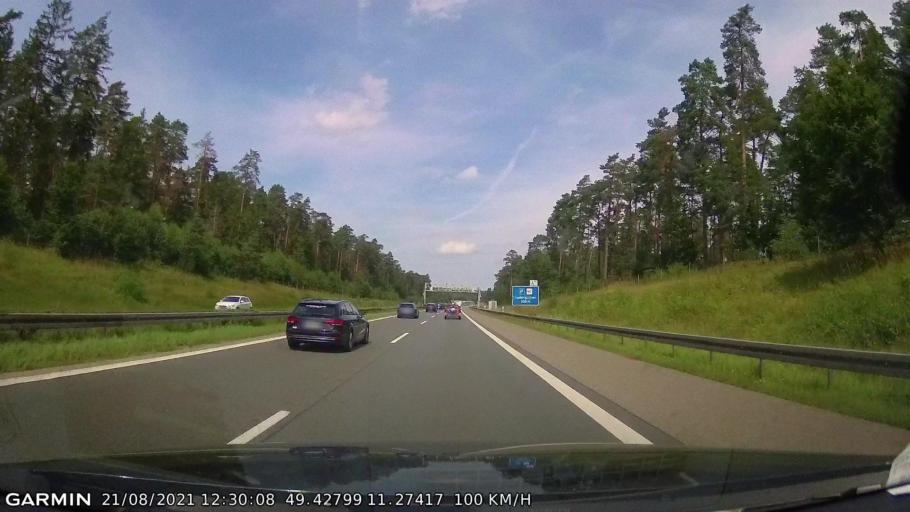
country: DE
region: Bavaria
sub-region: Regierungsbezirk Mittelfranken
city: Leinburg
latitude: 49.4280
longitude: 11.2742
